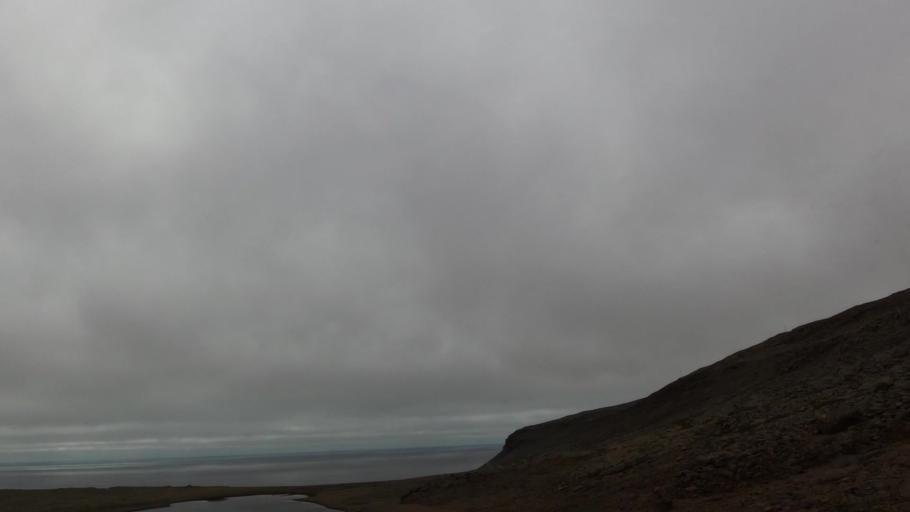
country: IS
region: West
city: Olafsvik
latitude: 65.5254
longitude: -24.4253
